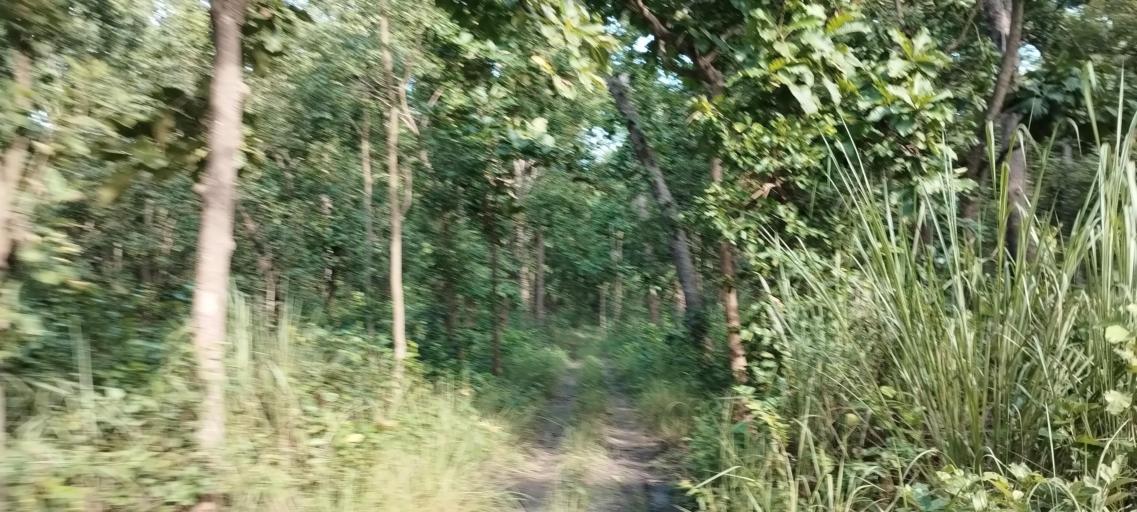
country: NP
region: Far Western
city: Tikapur
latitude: 28.5504
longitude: 81.2859
